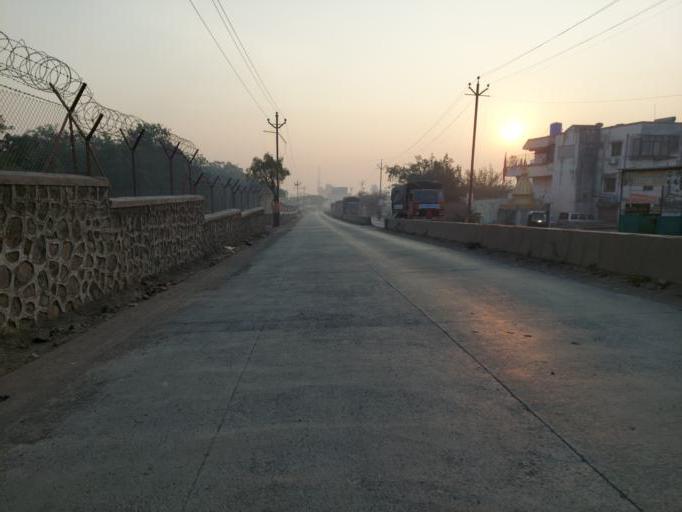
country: IN
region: Maharashtra
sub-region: Pune Division
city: Pune
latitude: 18.4664
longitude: 73.9569
